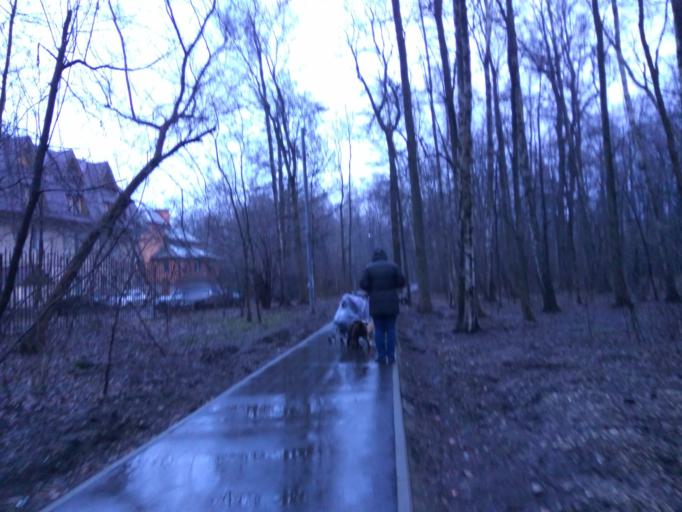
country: RU
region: Moscow
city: Vagonoremont
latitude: 55.9011
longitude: 37.5586
